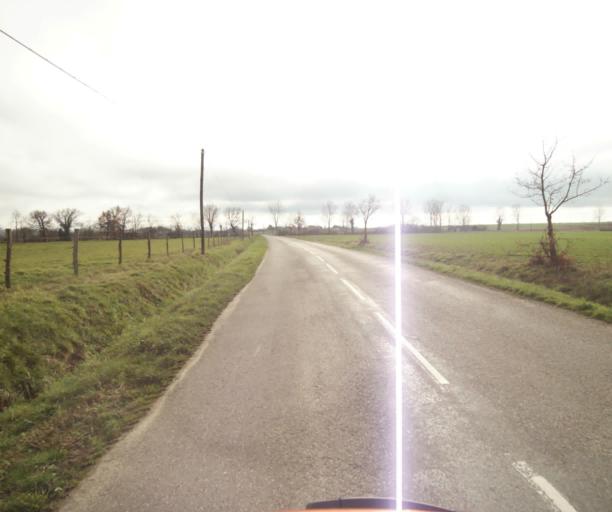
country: FR
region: Languedoc-Roussillon
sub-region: Departement de l'Aude
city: Belpech
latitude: 43.1945
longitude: 1.7297
